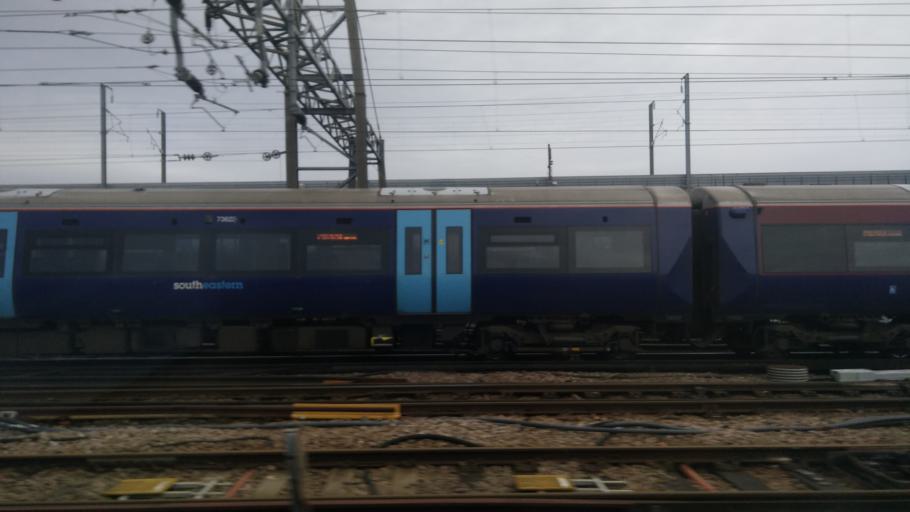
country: GB
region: England
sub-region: Kent
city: Ashford
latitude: 51.1411
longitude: 0.8796
